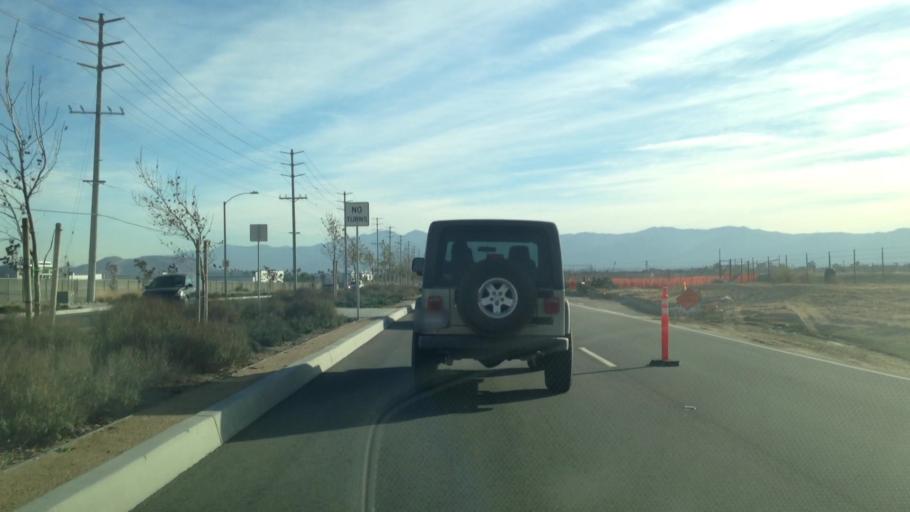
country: US
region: California
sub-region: Riverside County
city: Mira Loma
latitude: 33.9957
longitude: -117.5584
